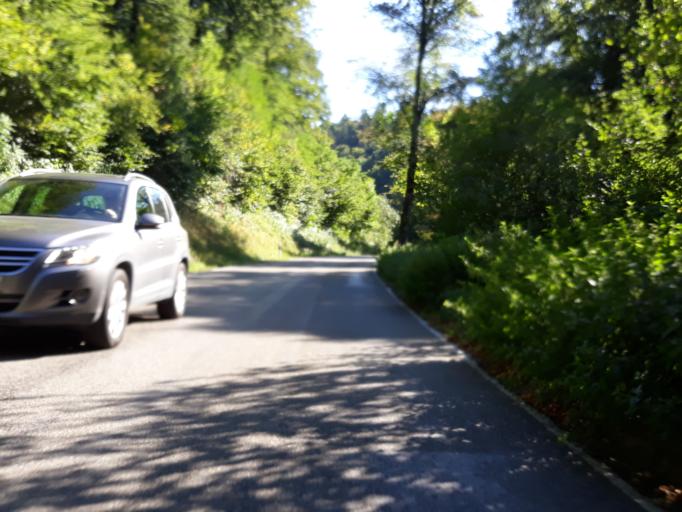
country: DE
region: Baden-Wuerttemberg
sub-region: Regierungsbezirk Stuttgart
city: Aidlingen
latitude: 48.6697
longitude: 8.9144
